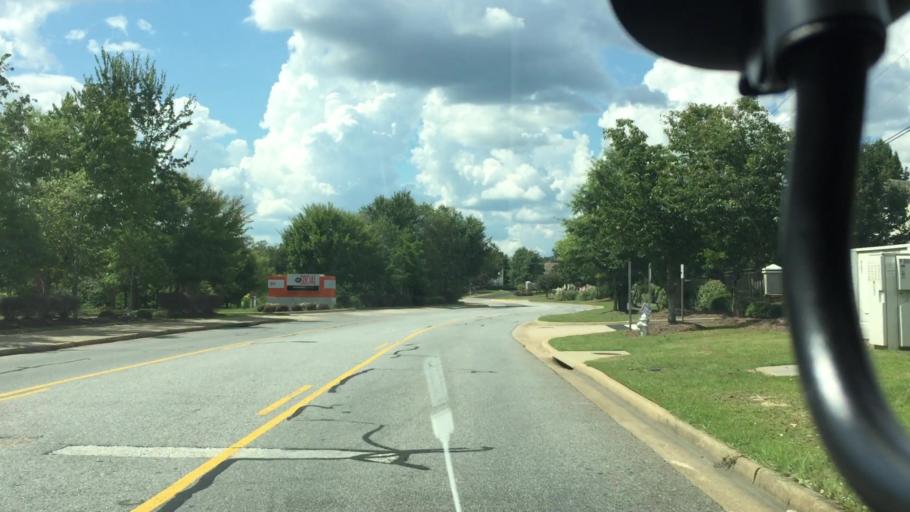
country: US
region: Alabama
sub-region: Lee County
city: Auburn
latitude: 32.5738
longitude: -85.5019
